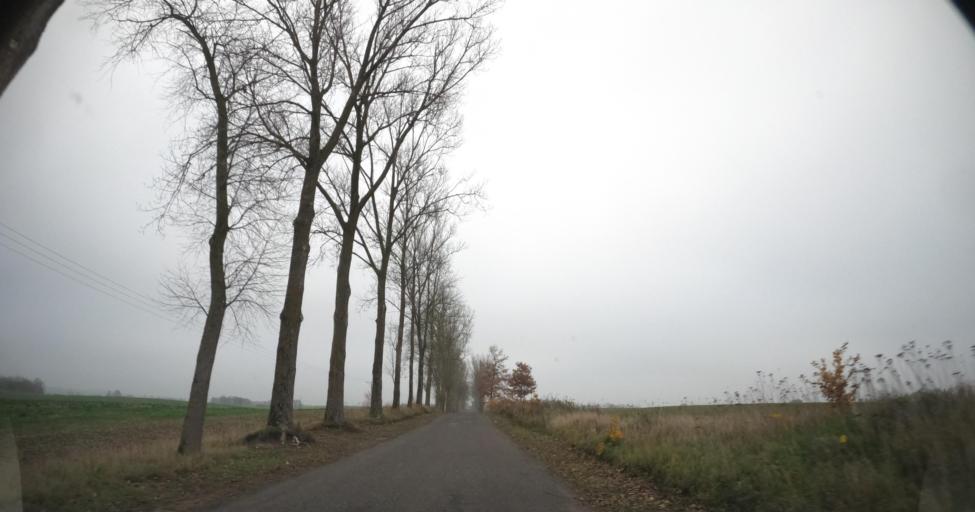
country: PL
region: West Pomeranian Voivodeship
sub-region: Powiat lobeski
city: Wegorzyno
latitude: 53.5433
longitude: 15.6316
